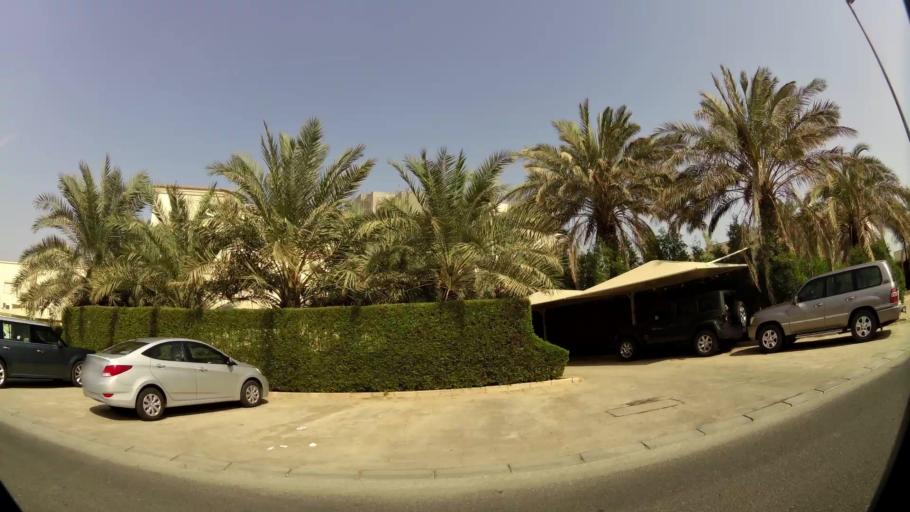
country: KW
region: Al Asimah
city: Ash Shamiyah
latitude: 29.3455
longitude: 47.9598
